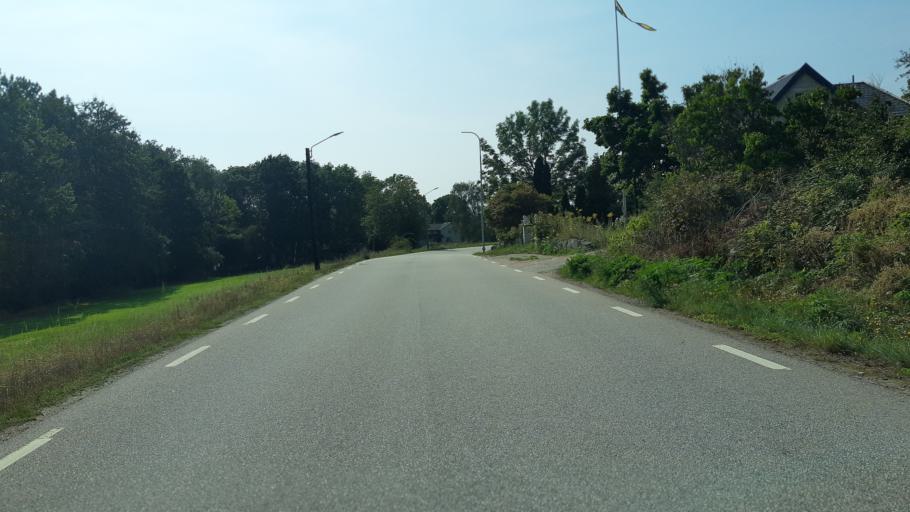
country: SE
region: Blekinge
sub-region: Ronneby Kommun
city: Ronneby
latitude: 56.1617
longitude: 15.2038
